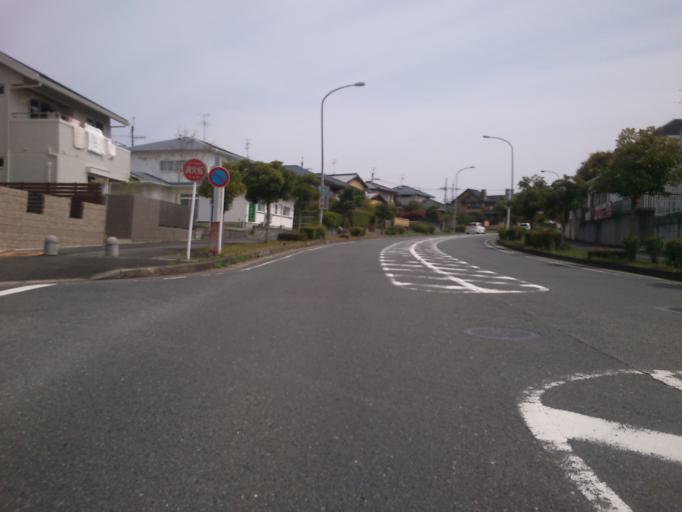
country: JP
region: Nara
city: Nara-shi
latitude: 34.7279
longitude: 135.7931
